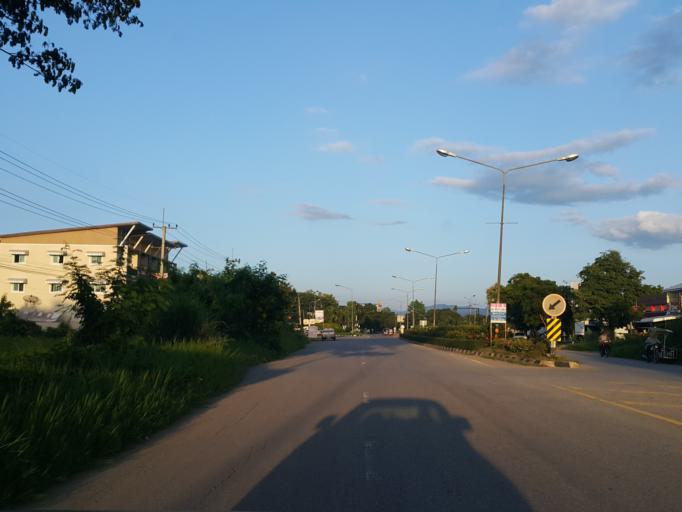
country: TH
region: Chiang Mai
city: San Kamphaeng
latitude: 18.7366
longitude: 99.1244
